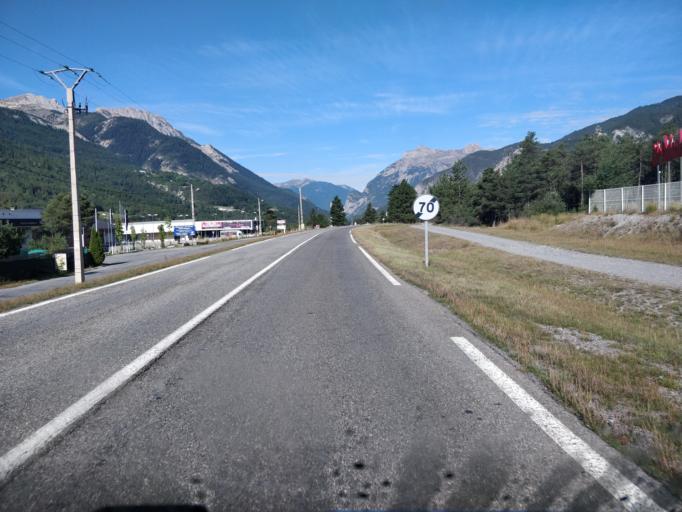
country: FR
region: Provence-Alpes-Cote d'Azur
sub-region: Departement des Alpes-de-Haute-Provence
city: Barcelonnette
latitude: 44.3855
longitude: 6.6068
